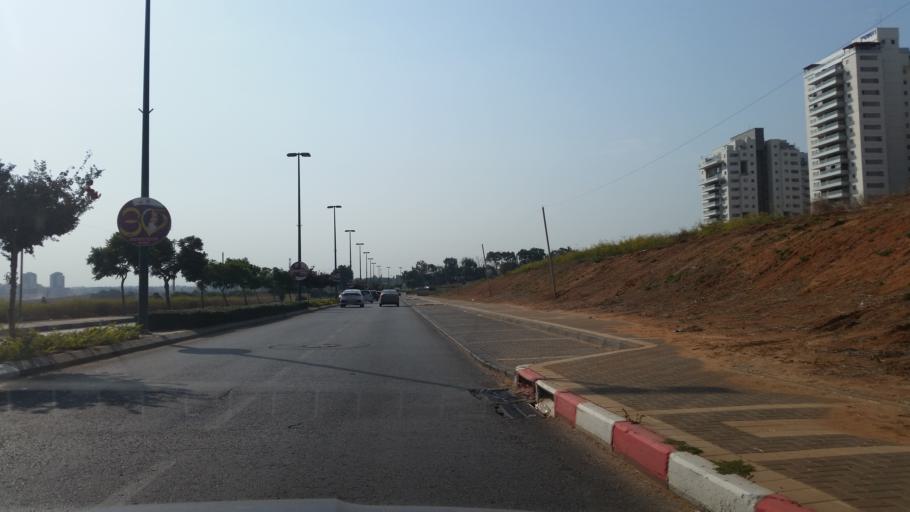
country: IL
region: Central District
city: Netanya
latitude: 32.3115
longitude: 34.8613
